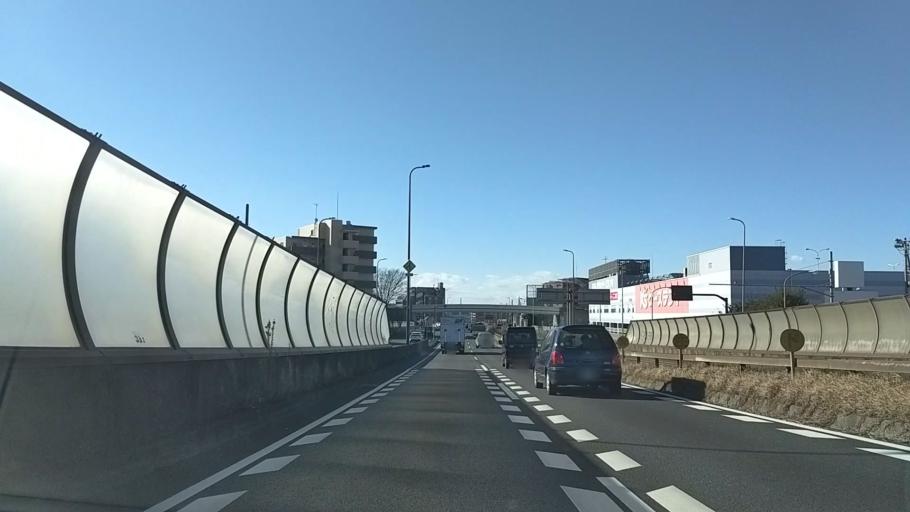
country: JP
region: Kanagawa
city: Minami-rinkan
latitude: 35.5084
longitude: 139.4749
